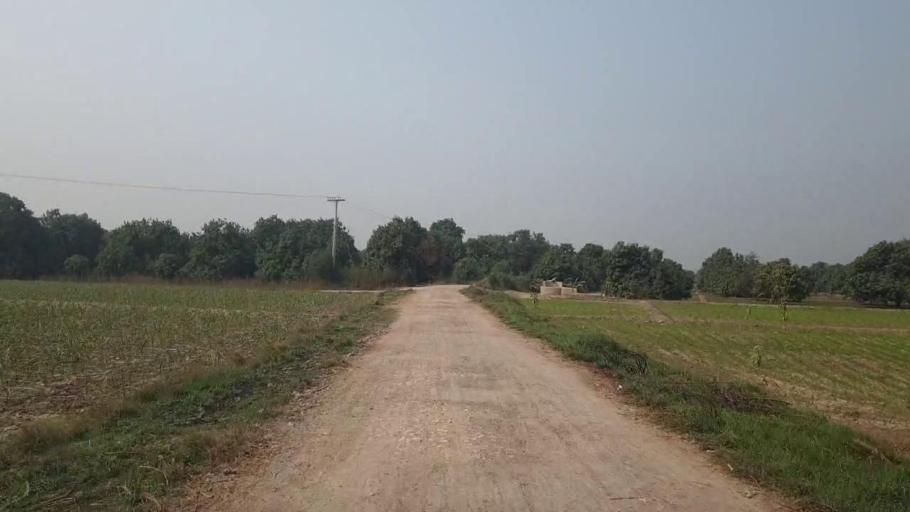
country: PK
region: Sindh
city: Tando Muhammad Khan
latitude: 25.2676
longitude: 68.5853
